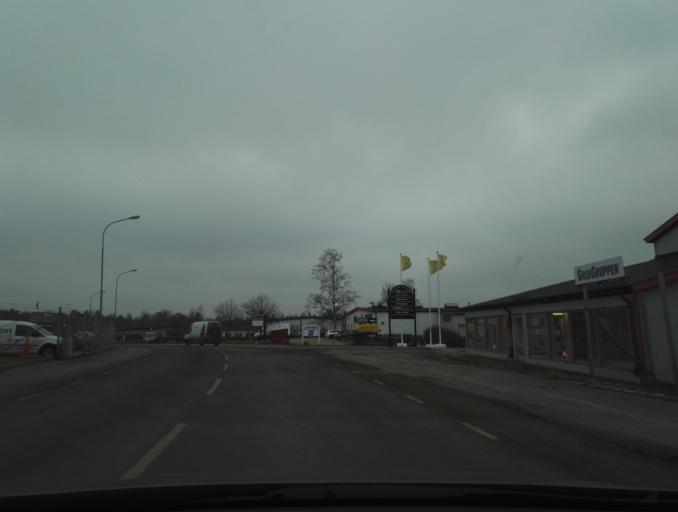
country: SE
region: Kronoberg
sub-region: Vaxjo Kommun
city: Vaexjoe
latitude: 56.8893
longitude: 14.7619
